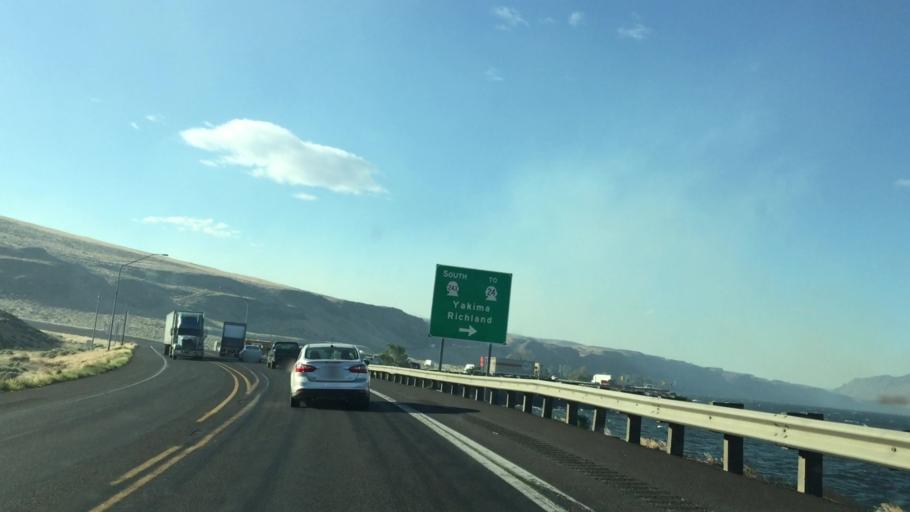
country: US
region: Washington
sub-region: Grant County
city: Mattawa
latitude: 46.9321
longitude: -119.9583
